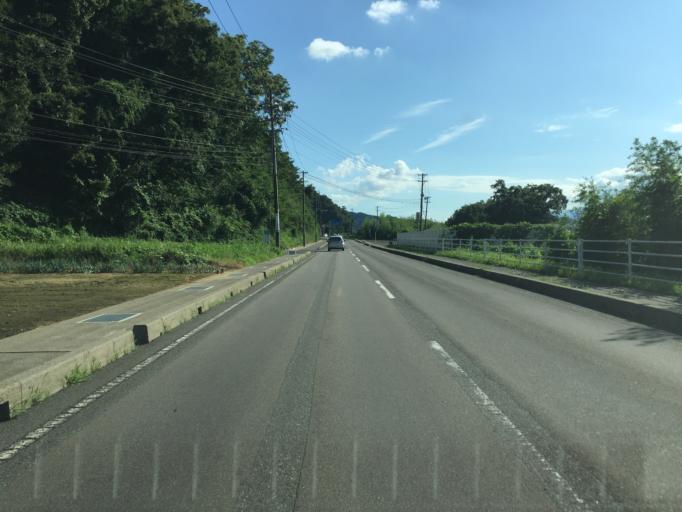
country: JP
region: Fukushima
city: Fukushima-shi
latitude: 37.7611
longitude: 140.4901
